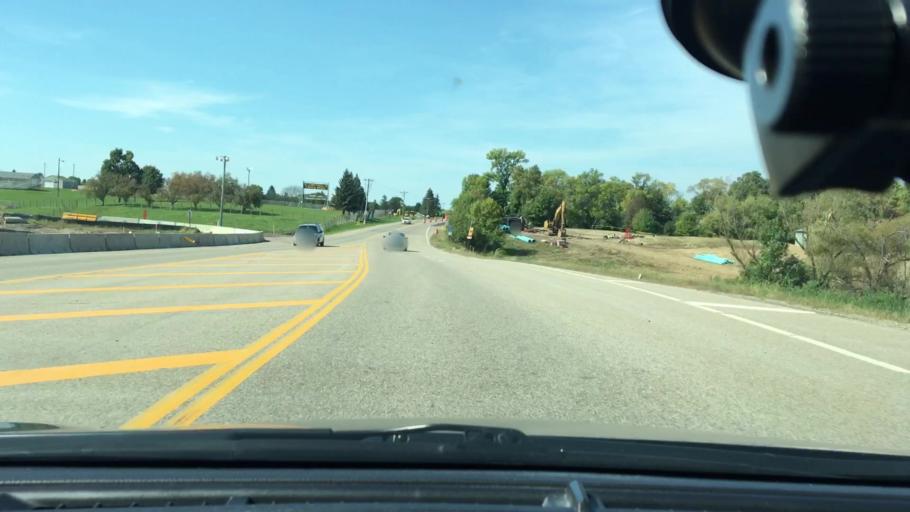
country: US
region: Minnesota
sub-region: Hennepin County
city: Corcoran
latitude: 45.0872
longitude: -93.5211
